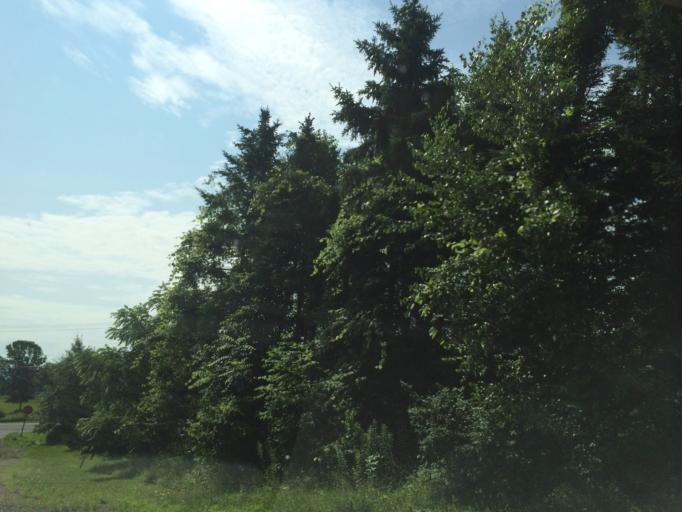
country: US
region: New York
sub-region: Orange County
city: Port Jervis
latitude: 41.3836
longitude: -74.6065
